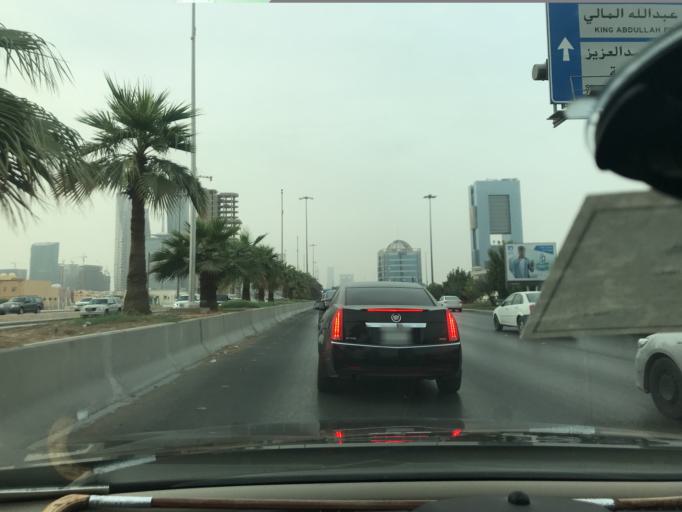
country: SA
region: Ar Riyad
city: Riyadh
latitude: 24.7519
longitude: 46.6520
